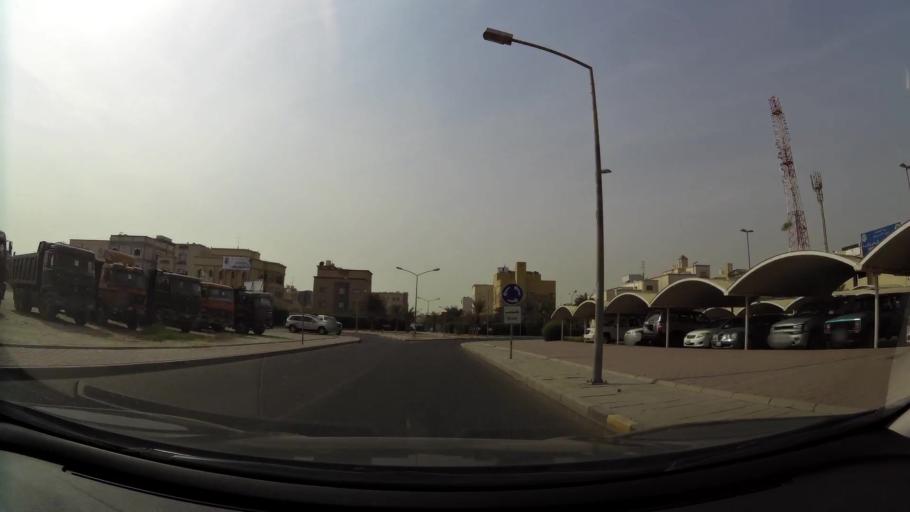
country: KW
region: Al Asimah
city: Ar Rabiyah
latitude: 29.2849
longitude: 47.9391
